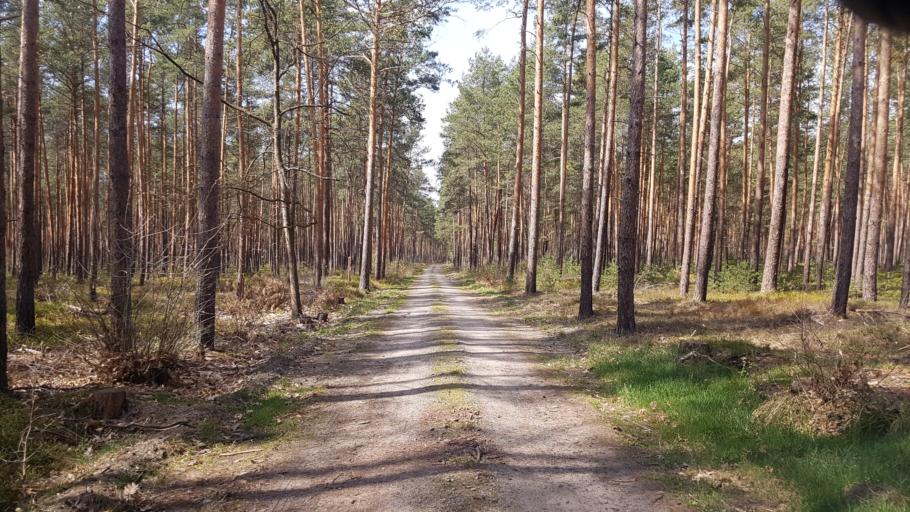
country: DE
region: Brandenburg
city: Plessa
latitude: 51.5462
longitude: 13.6568
